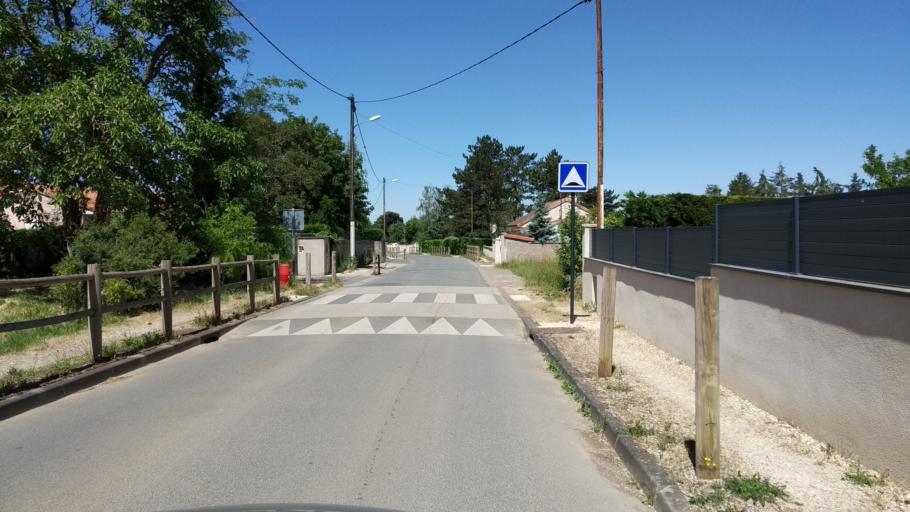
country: FR
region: Poitou-Charentes
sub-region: Departement de la Vienne
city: Vouneuil-sous-Biard
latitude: 46.5981
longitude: 0.2823
